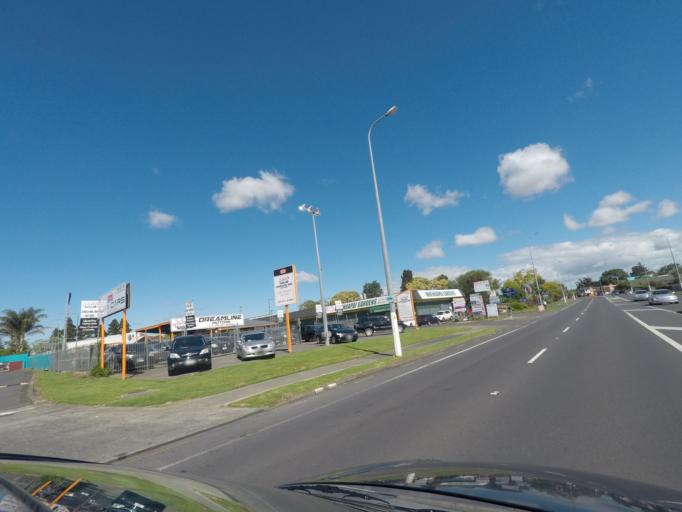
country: NZ
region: Auckland
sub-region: Auckland
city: Manukau City
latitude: -36.9808
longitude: 174.8767
